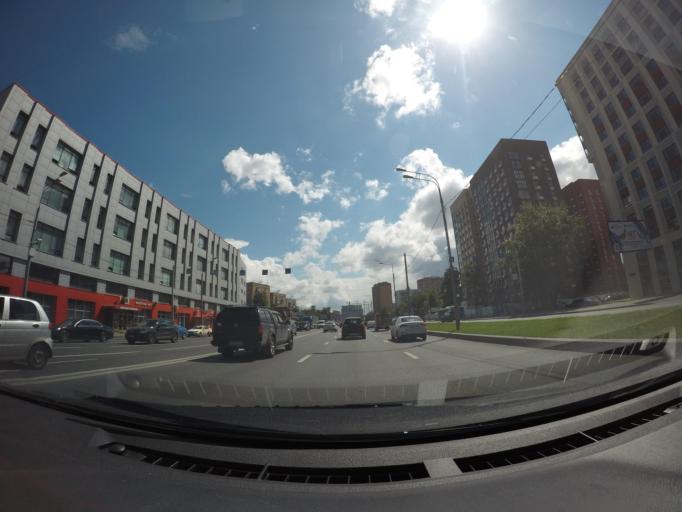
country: RU
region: Moscow
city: Lefortovo
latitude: 55.7331
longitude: 37.7129
